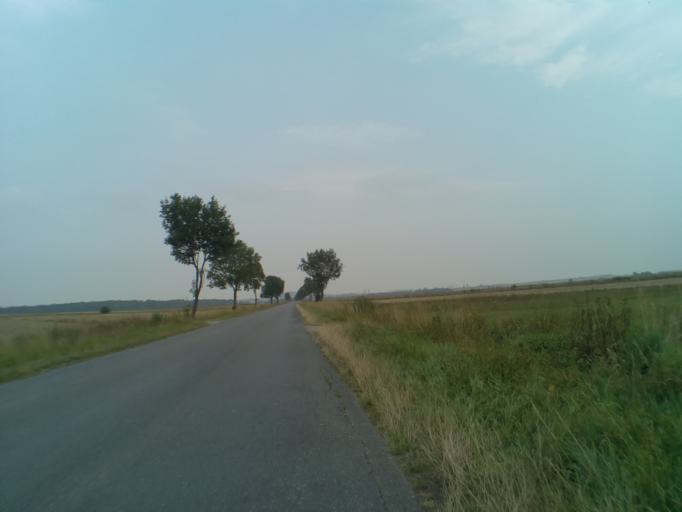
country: PL
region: Lower Silesian Voivodeship
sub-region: Powiat swidnicki
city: Strzegom
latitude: 50.9175
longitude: 16.3218
